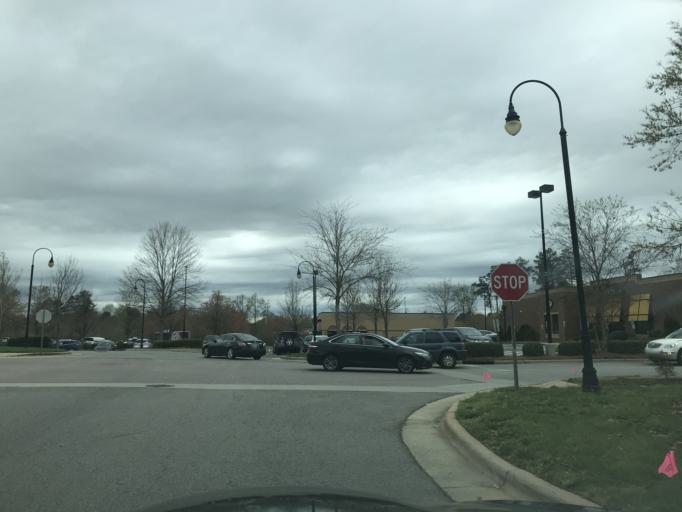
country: US
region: North Carolina
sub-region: Wake County
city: Morrisville
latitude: 35.9031
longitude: -78.7868
